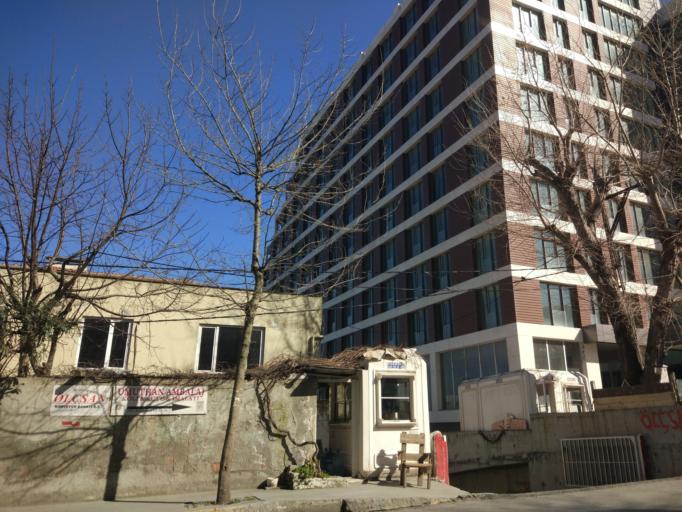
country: TR
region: Istanbul
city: Mahmutbey
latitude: 41.0176
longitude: 28.8042
